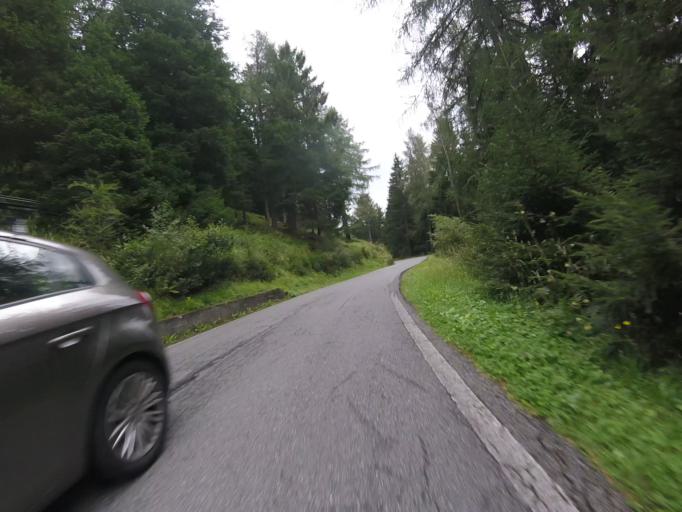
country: IT
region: Lombardy
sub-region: Provincia di Brescia
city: Monno
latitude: 46.2302
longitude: 10.3219
